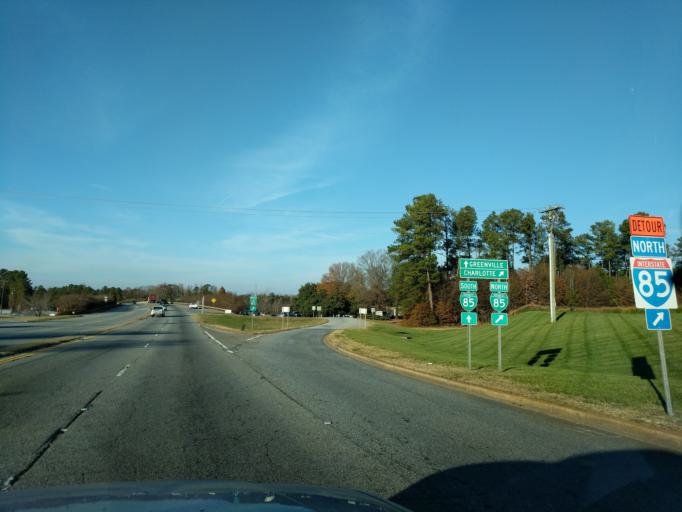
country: US
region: South Carolina
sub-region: Spartanburg County
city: Valley Falls
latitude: 34.9922
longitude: -81.9465
